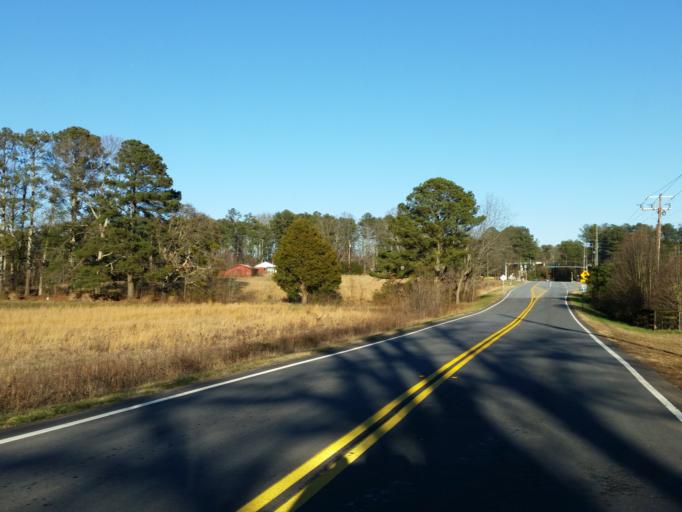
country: US
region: Georgia
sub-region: Cobb County
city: Acworth
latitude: 33.9743
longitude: -84.7167
